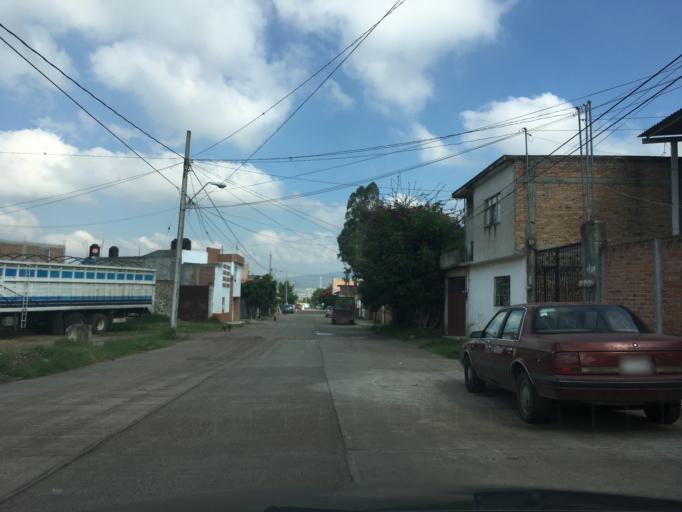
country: MX
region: Michoacan
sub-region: Morelia
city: Morelos
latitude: 19.6483
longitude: -101.2314
